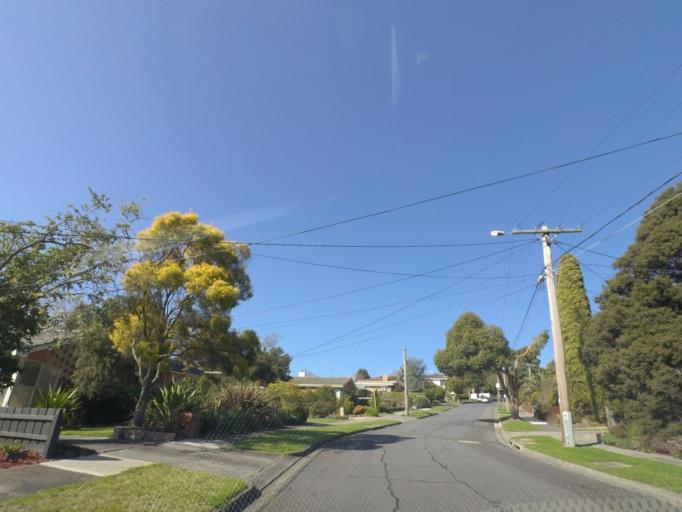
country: AU
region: Victoria
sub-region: Manningham
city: Templestowe Lower
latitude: -37.7674
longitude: 145.1160
